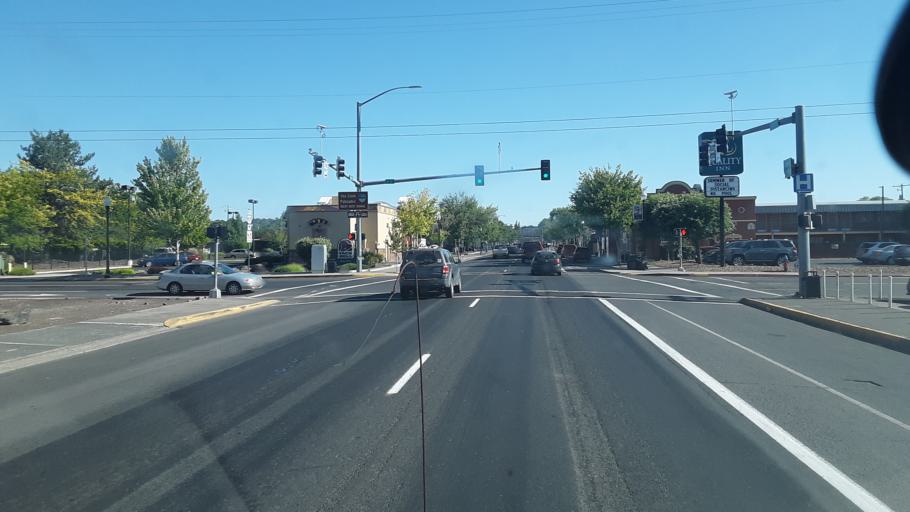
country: US
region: Oregon
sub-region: Jefferson County
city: Madras
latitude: 44.6363
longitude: -121.1306
